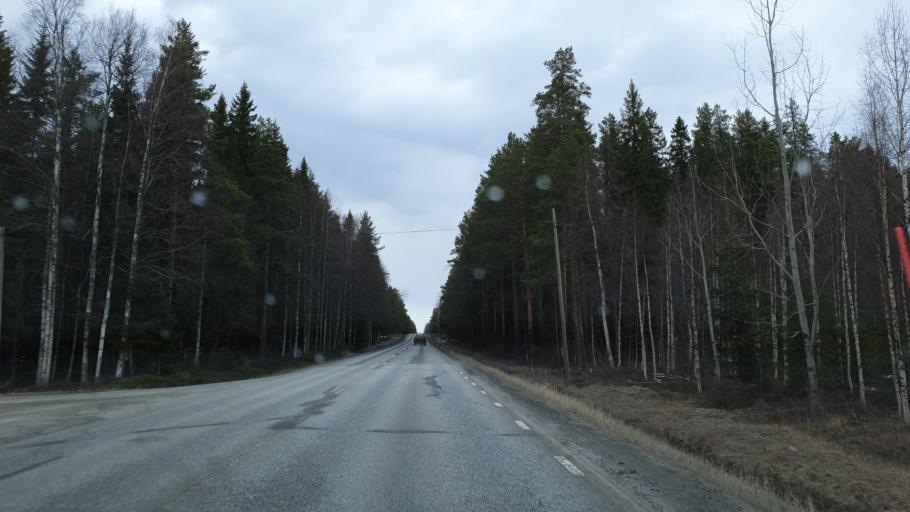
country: SE
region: Vaesterbotten
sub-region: Skelleftea Kommun
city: Viken
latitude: 64.6535
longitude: 20.9547
